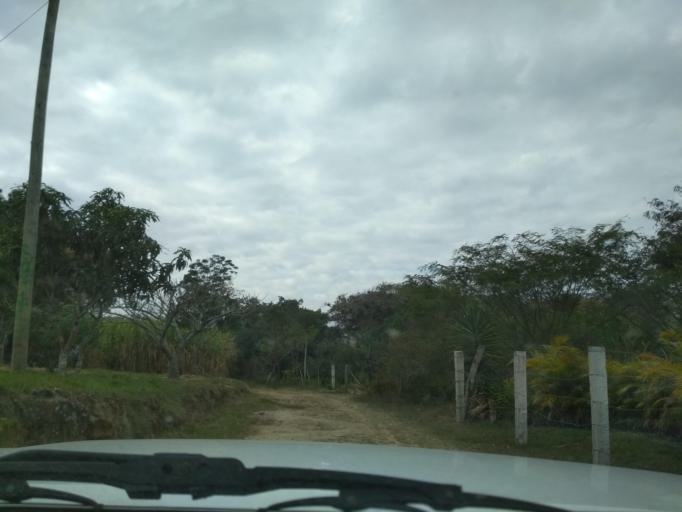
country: MX
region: Veracruz
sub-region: Coatepec
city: Tuzamapan
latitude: 19.3684
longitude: -96.8830
